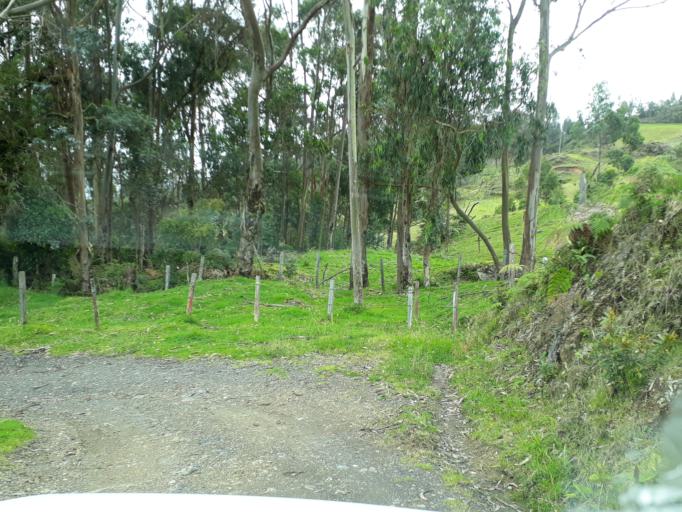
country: CO
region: Cundinamarca
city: Junin
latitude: 4.7400
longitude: -73.6251
